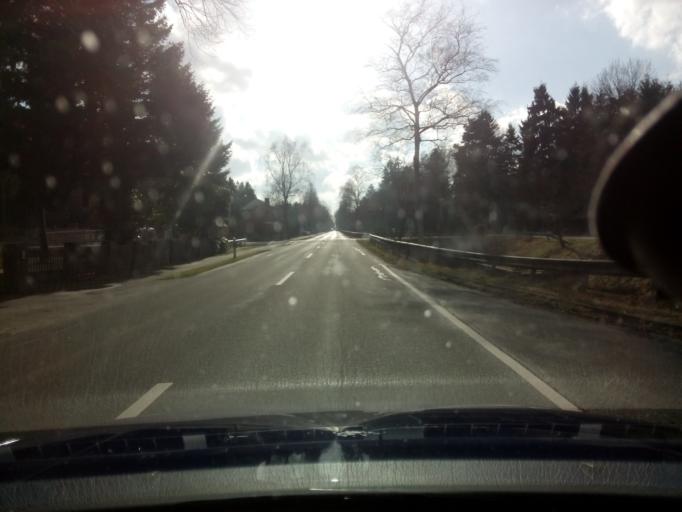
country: DE
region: Lower Saxony
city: Gnarrenburg
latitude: 53.3982
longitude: 9.0329
